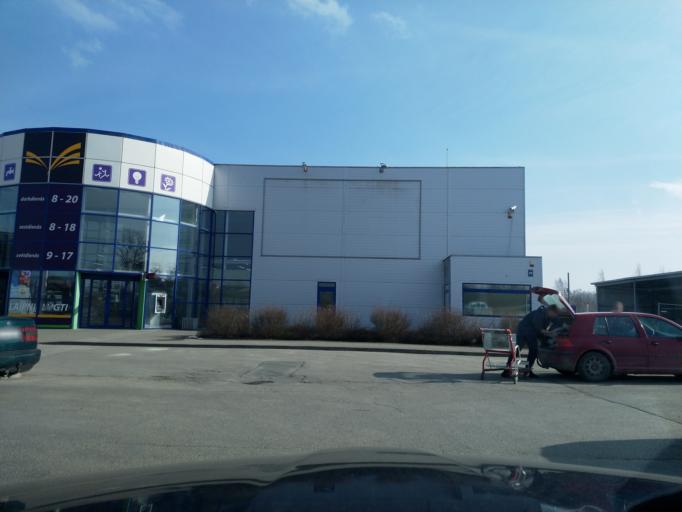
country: LV
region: Kuldigas Rajons
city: Kuldiga
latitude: 56.9575
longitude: 21.9905
